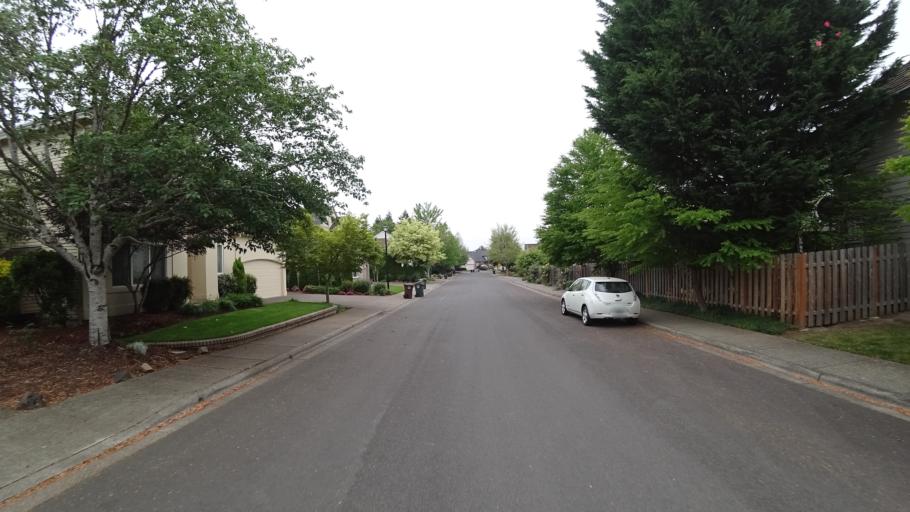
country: US
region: Oregon
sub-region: Washington County
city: Bethany
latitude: 45.5465
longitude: -122.8605
